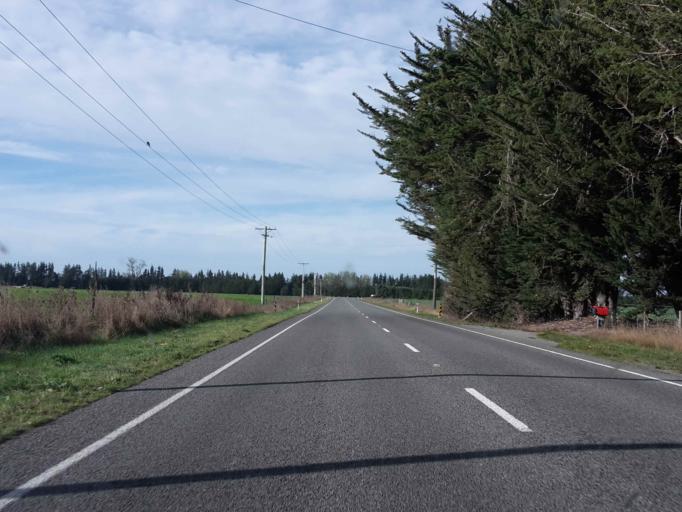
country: NZ
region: Canterbury
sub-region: Timaru District
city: Pleasant Point
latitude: -44.0441
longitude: 171.2786
